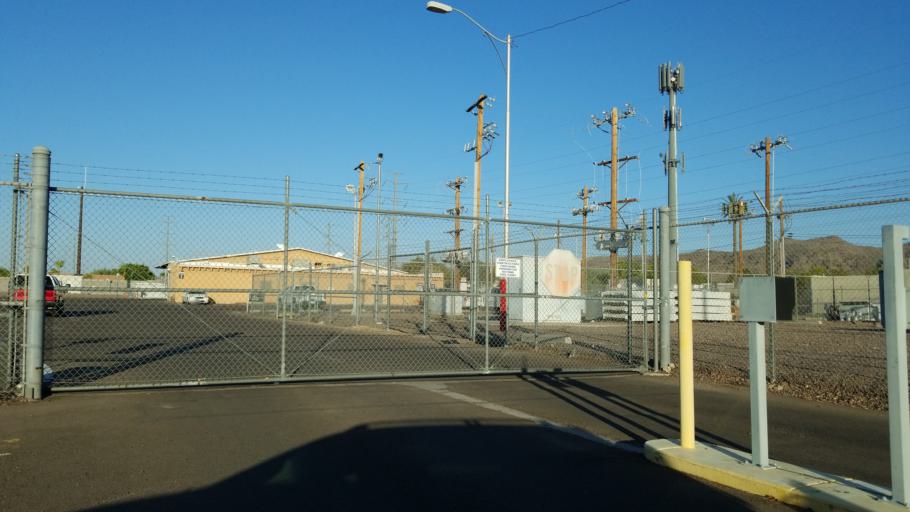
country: US
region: Arizona
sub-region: Maricopa County
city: Phoenix
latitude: 33.3804
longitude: -112.0469
